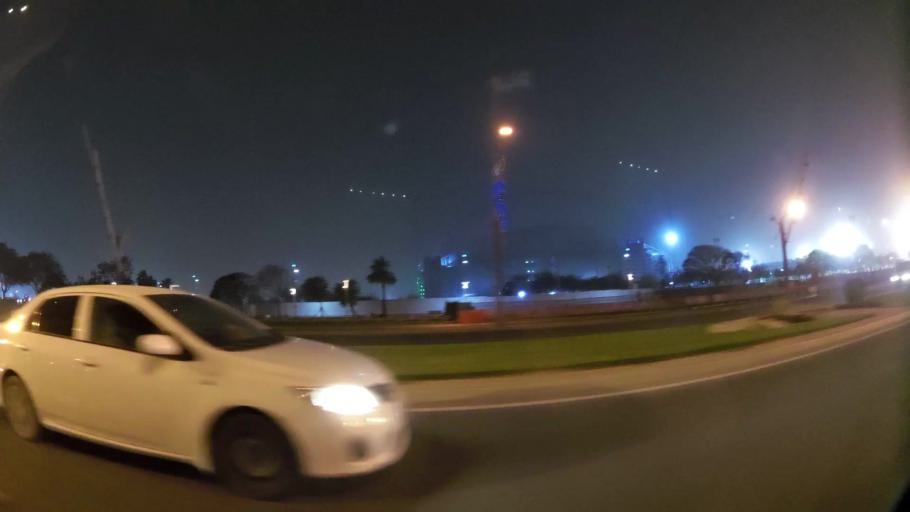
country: QA
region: Baladiyat ar Rayyan
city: Ar Rayyan
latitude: 25.2642
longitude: 51.4529
